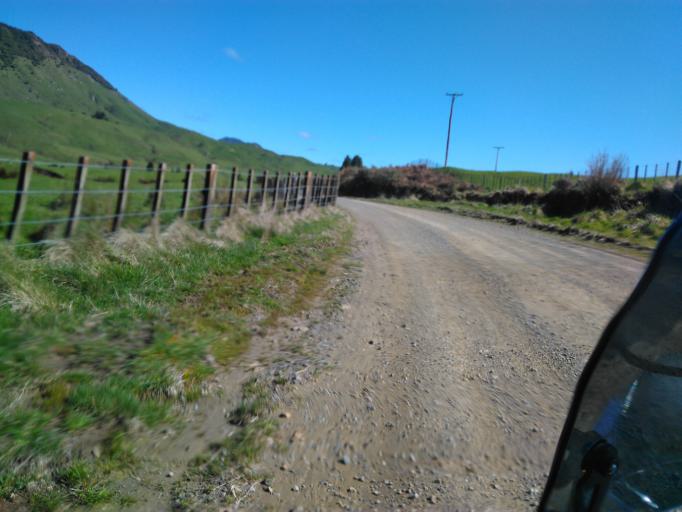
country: NZ
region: Bay of Plenty
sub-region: Opotiki District
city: Opotiki
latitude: -38.3095
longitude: 177.5641
